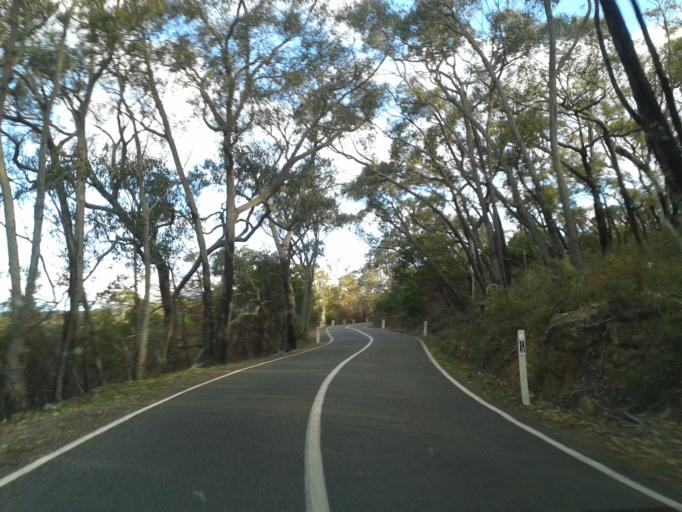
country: AU
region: Victoria
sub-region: Northern Grampians
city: Stawell
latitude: -37.1372
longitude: 142.4370
